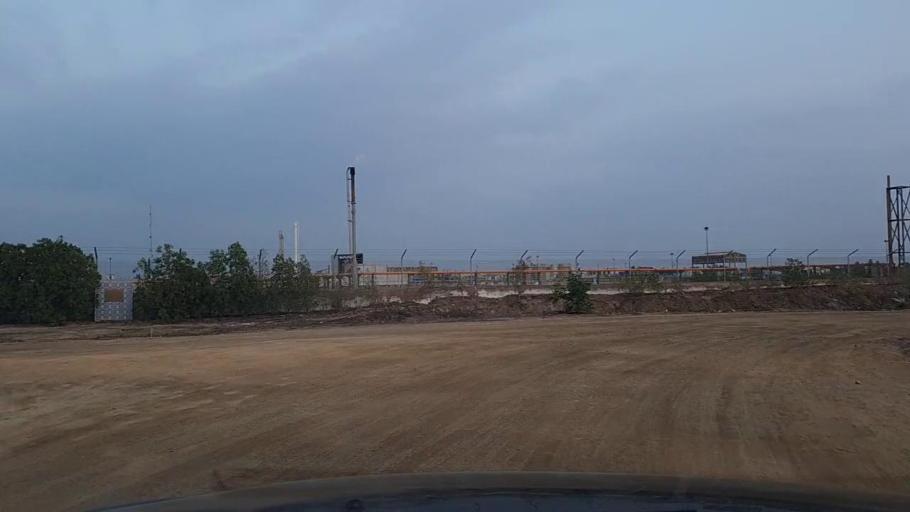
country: PK
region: Sindh
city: Jati
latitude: 24.4913
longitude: 68.3916
